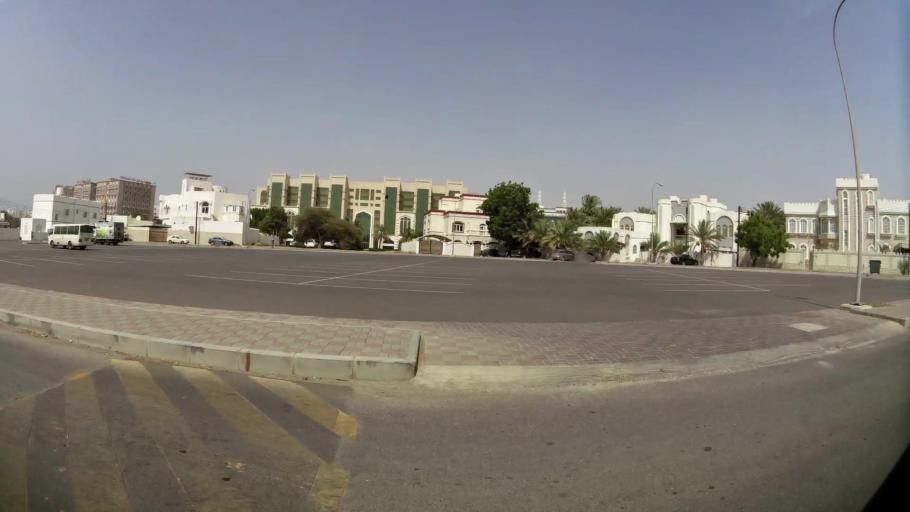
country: OM
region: Muhafazat Masqat
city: Bawshar
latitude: 23.5793
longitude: 58.4061
